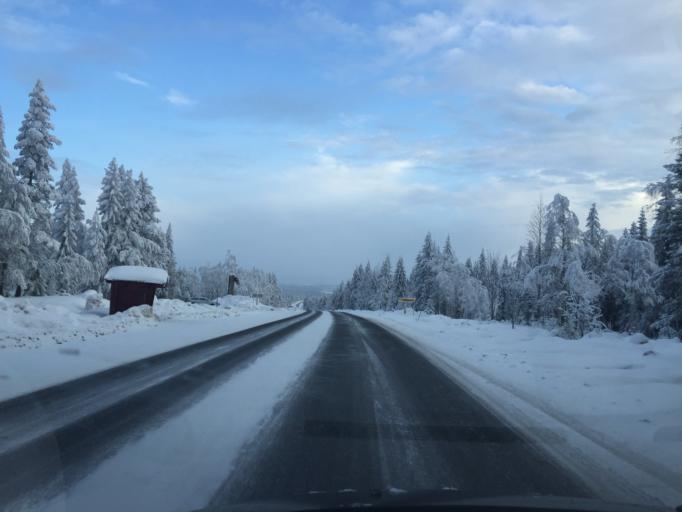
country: NO
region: Hedmark
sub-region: Valer
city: Valer
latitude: 61.0506
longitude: 11.9360
